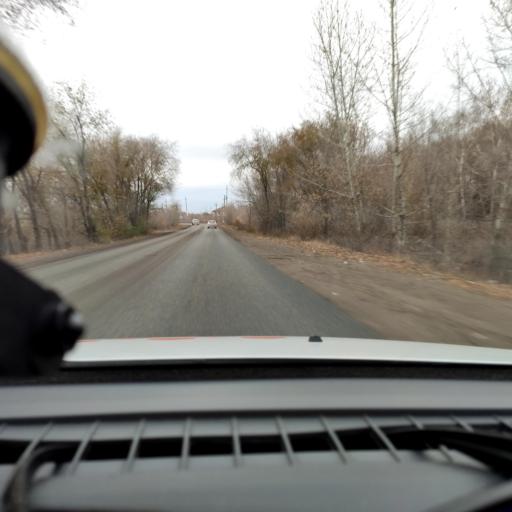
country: RU
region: Samara
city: Samara
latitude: 53.1261
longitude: 50.2357
